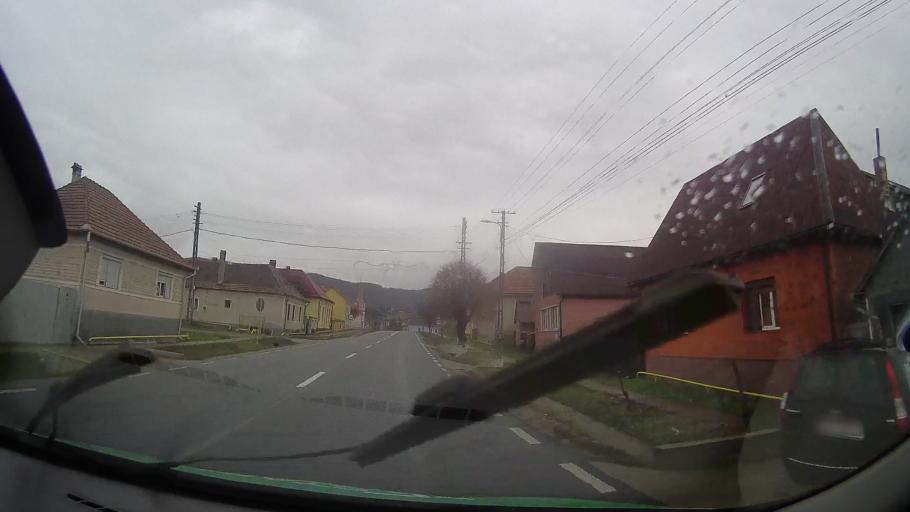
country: RO
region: Bistrita-Nasaud
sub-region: Comuna Teaca
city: Teaca
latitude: 46.9125
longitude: 24.5022
